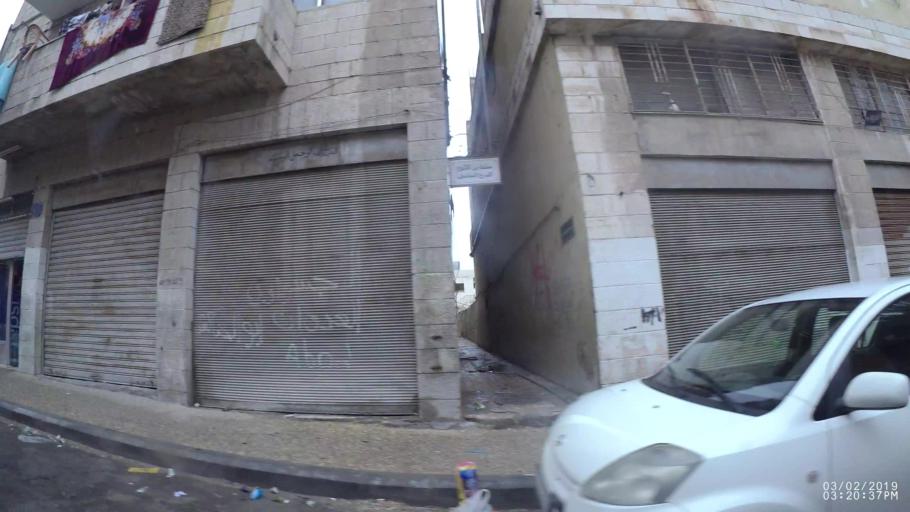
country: JO
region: Amman
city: Amman
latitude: 31.9545
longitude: 35.9423
